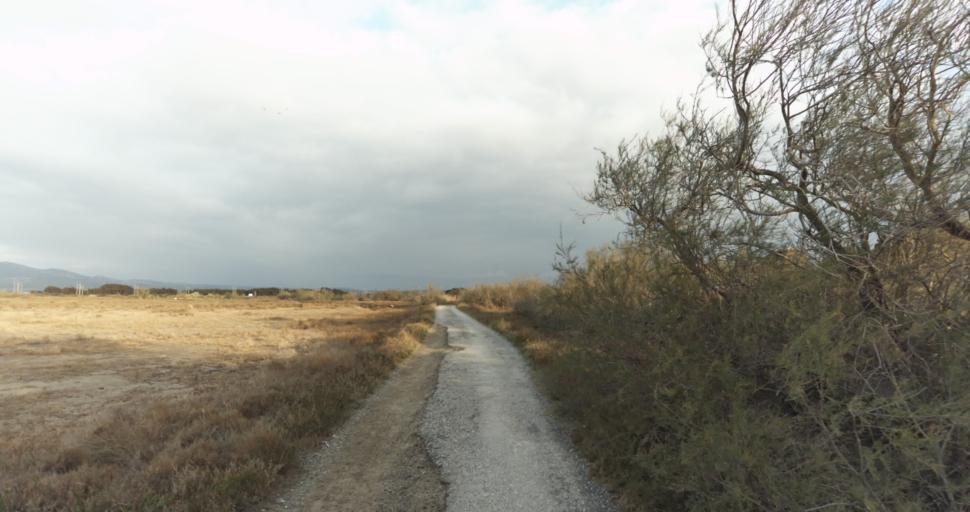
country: FR
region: Languedoc-Roussillon
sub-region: Departement de l'Aude
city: Leucate
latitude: 42.9526
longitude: 3.0324
